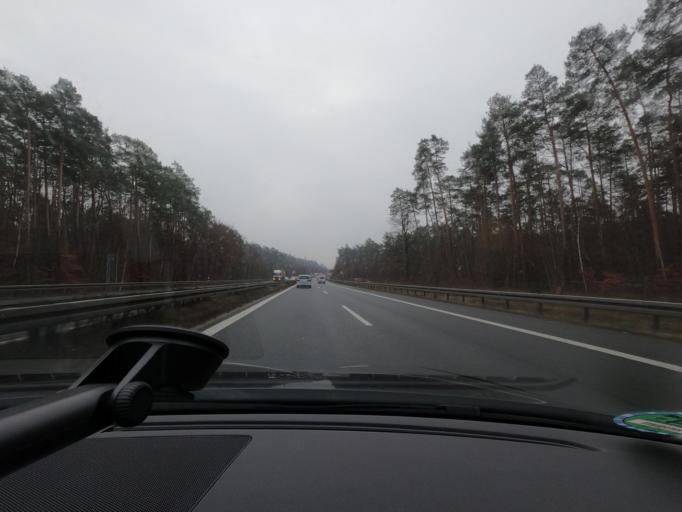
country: DE
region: Bavaria
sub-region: Upper Franconia
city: Memmelsdorf
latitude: 49.8976
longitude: 10.9481
